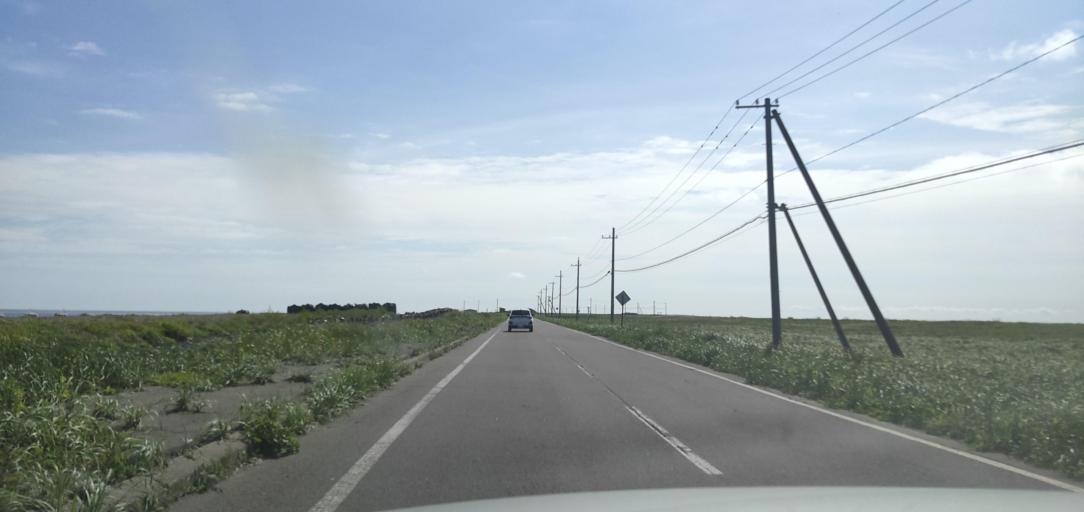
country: JP
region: Hokkaido
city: Shibetsu
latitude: 43.6274
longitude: 145.2006
